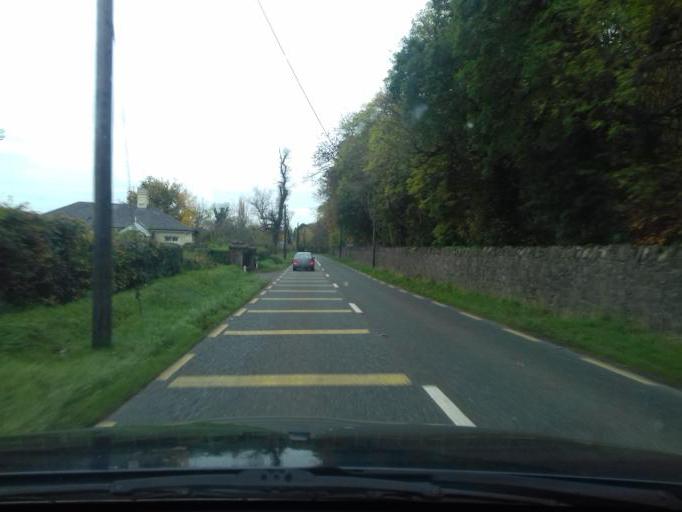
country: IE
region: Leinster
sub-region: Kildare
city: Maynooth
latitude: 53.3978
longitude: -6.5633
